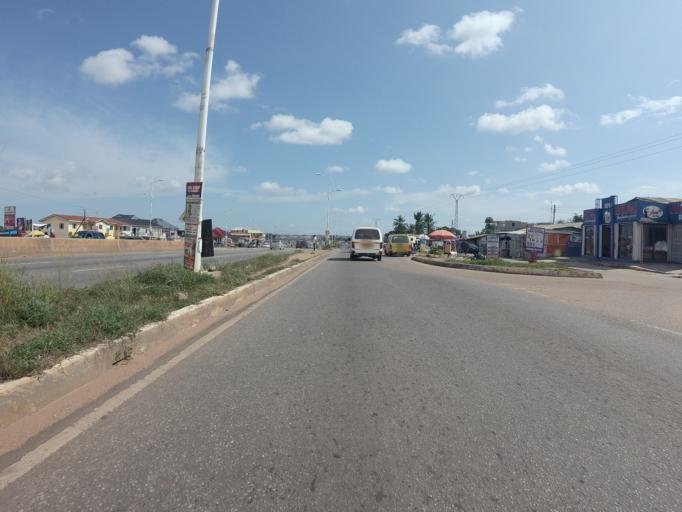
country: GH
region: Greater Accra
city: Medina Estates
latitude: 5.7005
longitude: -0.1719
